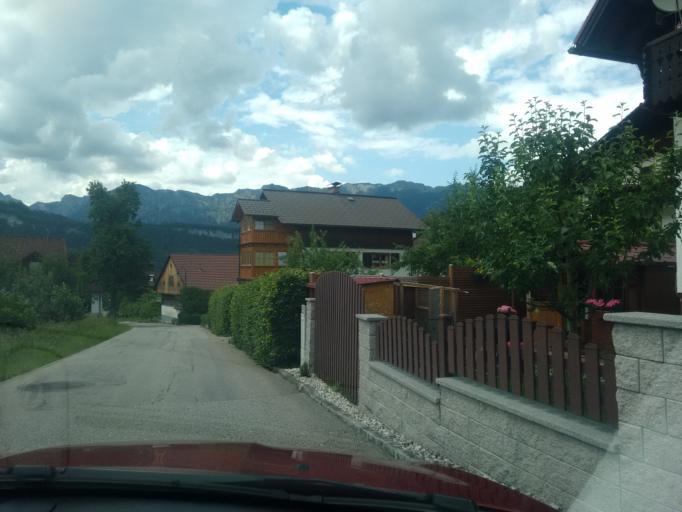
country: AT
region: Upper Austria
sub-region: Politischer Bezirk Gmunden
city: Bad Goisern
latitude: 47.6409
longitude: 13.6273
